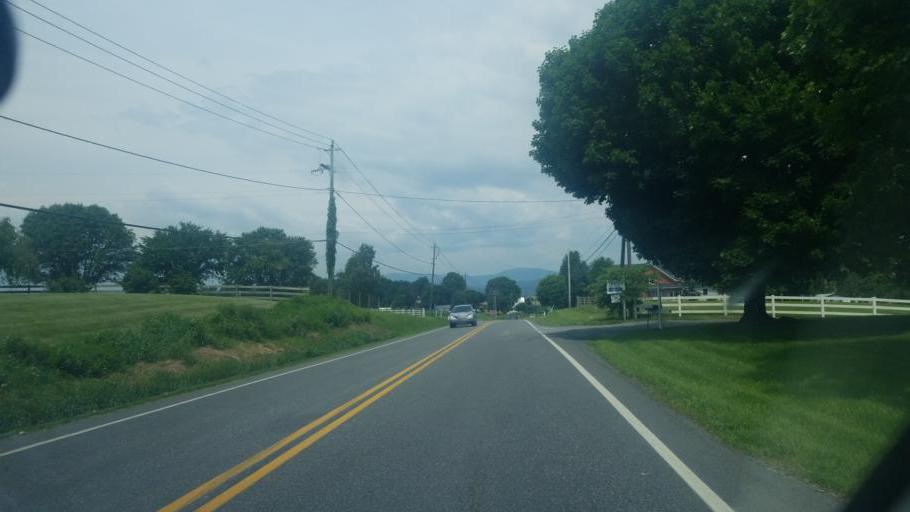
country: US
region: Virginia
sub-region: Rockingham County
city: Dayton
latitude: 38.4608
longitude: -78.9591
